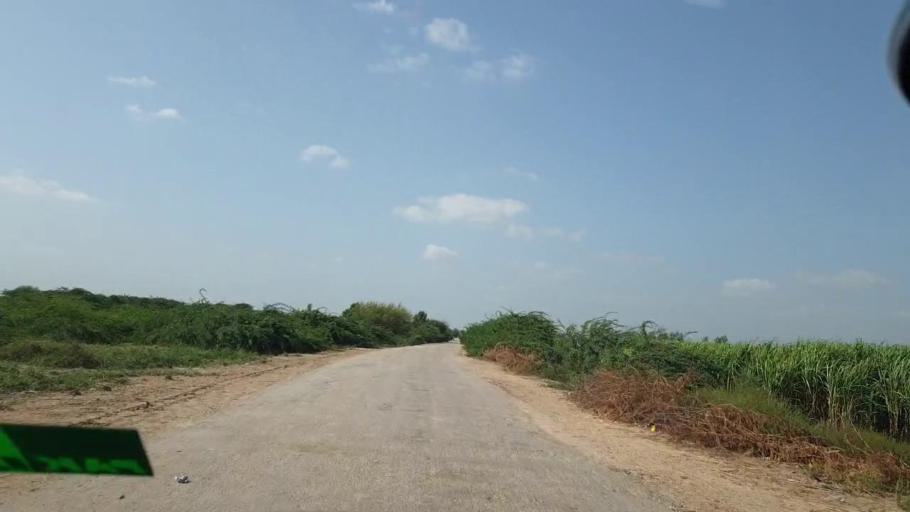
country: PK
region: Sindh
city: Tando Bago
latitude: 24.6764
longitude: 69.1920
